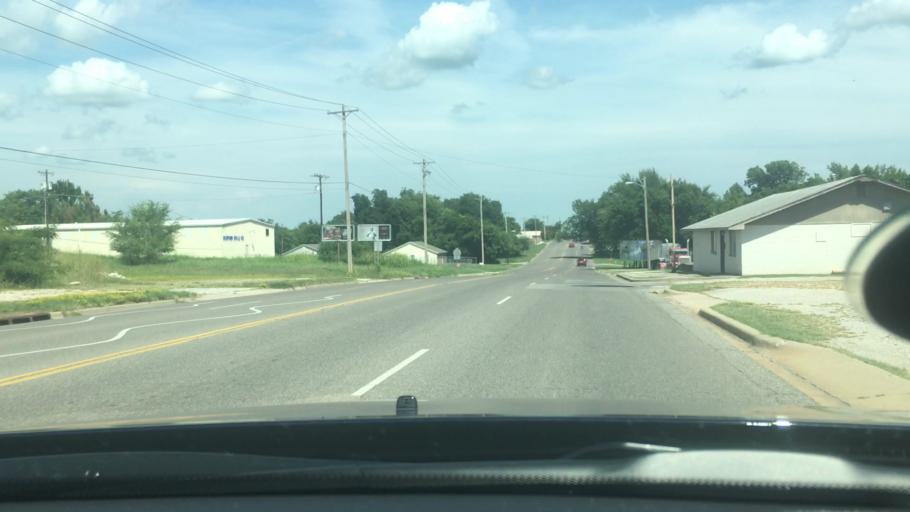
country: US
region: Oklahoma
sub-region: Pottawatomie County
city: Shawnee
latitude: 35.3327
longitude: -96.9032
